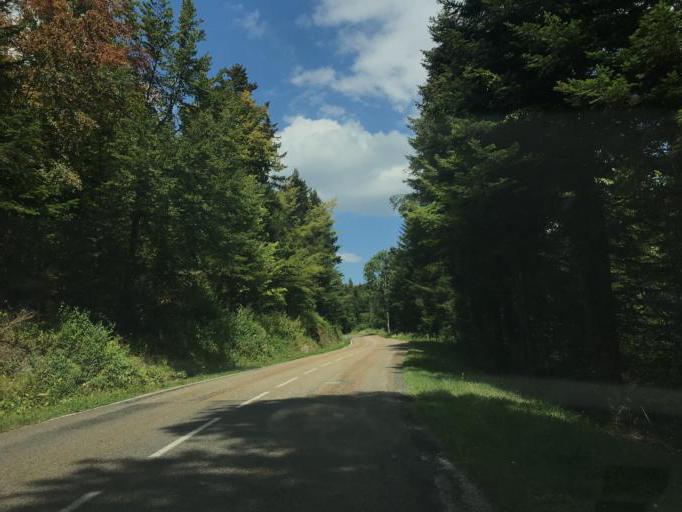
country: FR
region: Franche-Comte
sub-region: Departement du Jura
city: Clairvaux-les-Lacs
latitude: 46.5479
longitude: 5.7873
